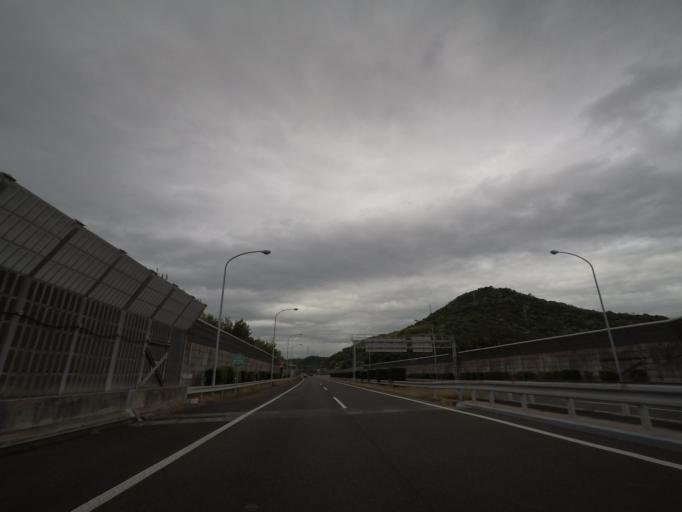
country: JP
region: Kagawa
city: Sakaidecho
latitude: 34.2989
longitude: 133.8434
